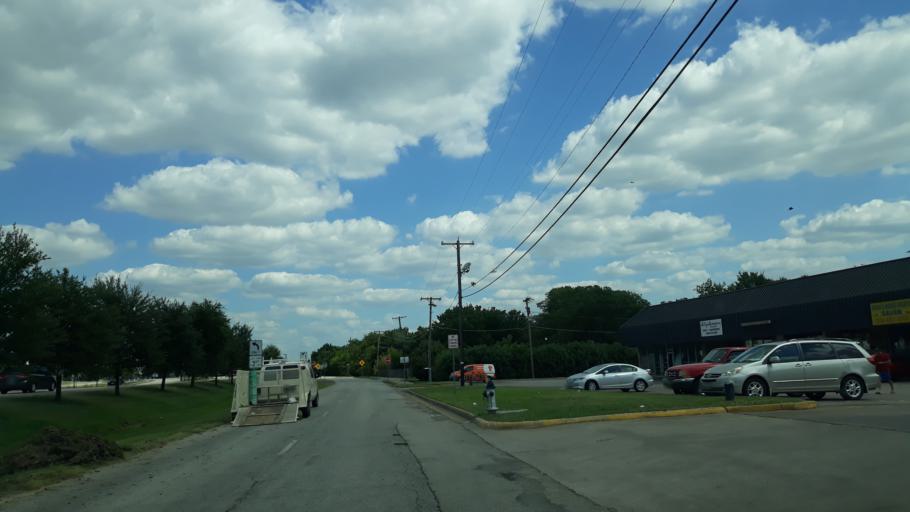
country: US
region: Texas
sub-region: Dallas County
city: Irving
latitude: 32.8335
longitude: -96.9883
